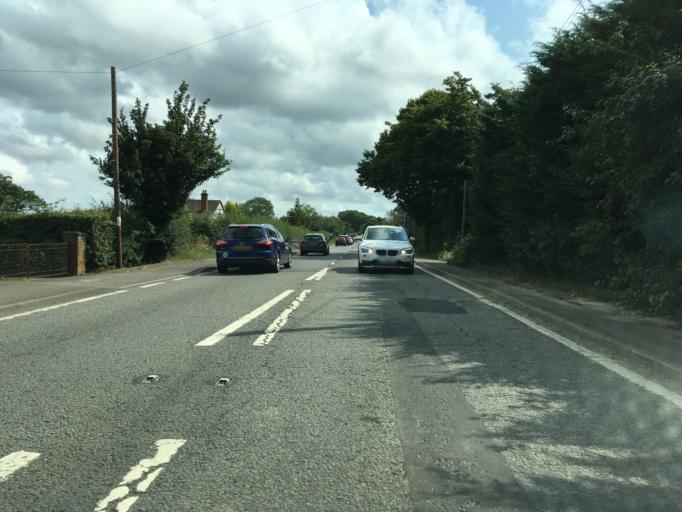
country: GB
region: England
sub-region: Kent
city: Tenterden
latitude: 51.0957
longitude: 0.6889
